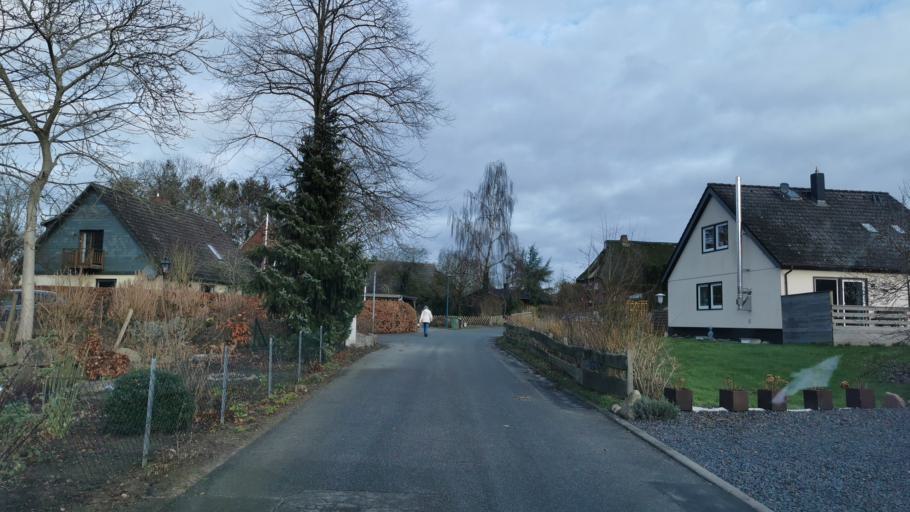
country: DE
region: Schleswig-Holstein
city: Pohnsdorf
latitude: 54.2375
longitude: 10.2484
